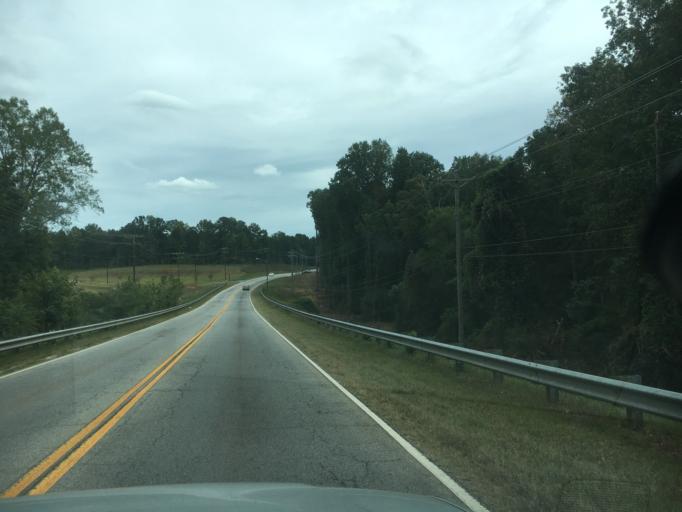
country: US
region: South Carolina
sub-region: Laurens County
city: Watts Mills
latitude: 34.5011
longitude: -81.9906
